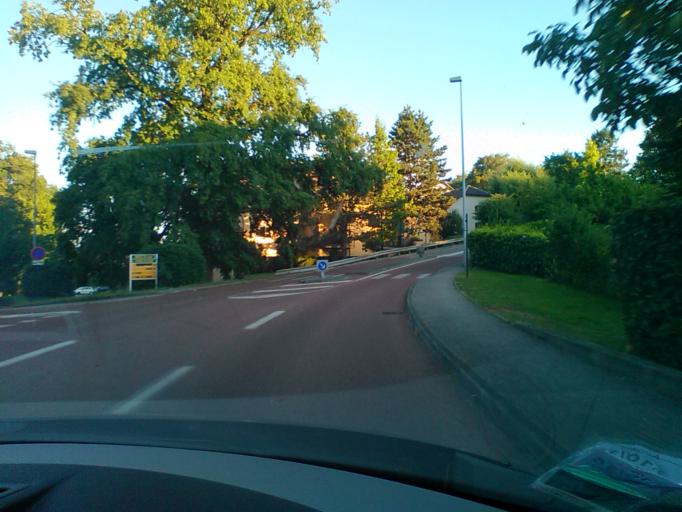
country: FR
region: Rhone-Alpes
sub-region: Departement de la Savoie
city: Chambery
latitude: 45.5608
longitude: 5.9422
